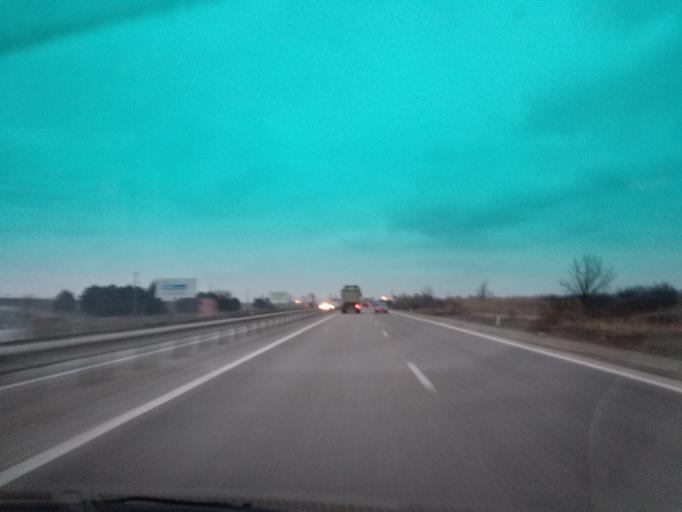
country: RU
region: Adygeya
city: Adygeysk
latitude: 44.9186
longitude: 39.1469
